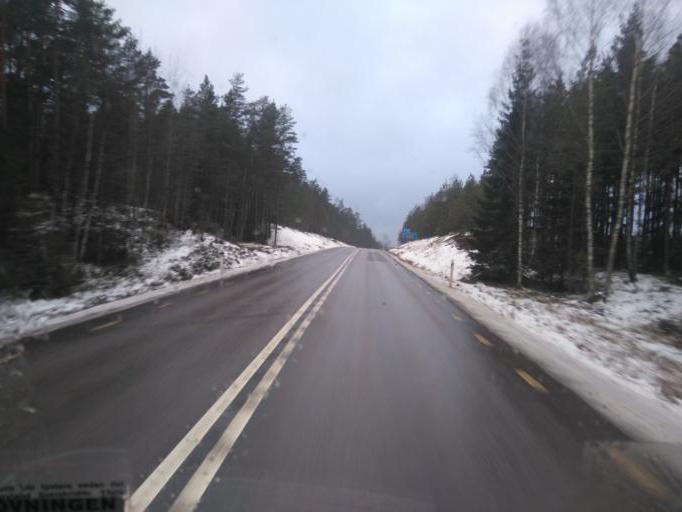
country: SE
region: Joenkoeping
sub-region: Eksjo Kommun
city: Mariannelund
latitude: 57.6257
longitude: 15.6077
